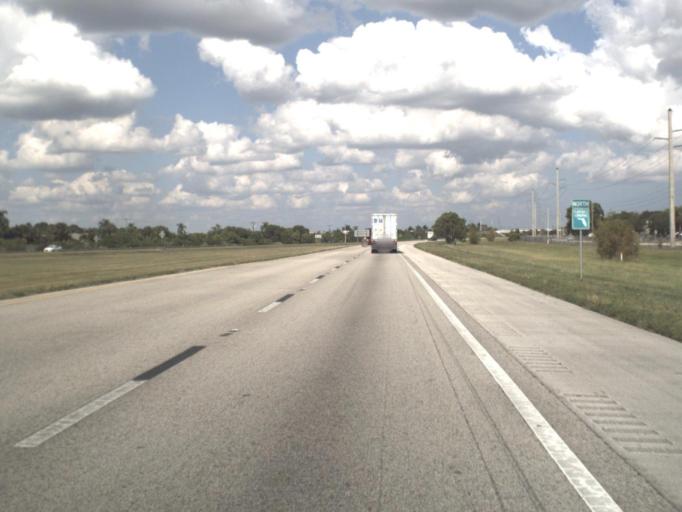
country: US
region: Florida
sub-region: Saint Lucie County
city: Port Saint Lucie
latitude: 27.3075
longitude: -80.3733
